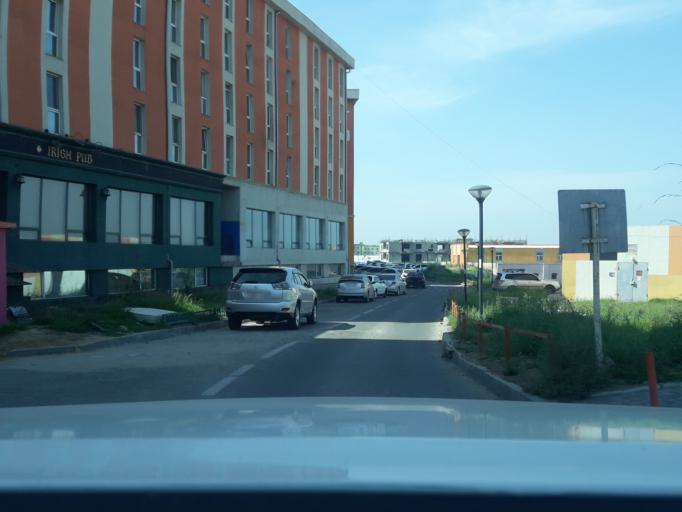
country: MN
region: Ulaanbaatar
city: Ulaanbaatar
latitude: 47.8818
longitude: 106.8520
